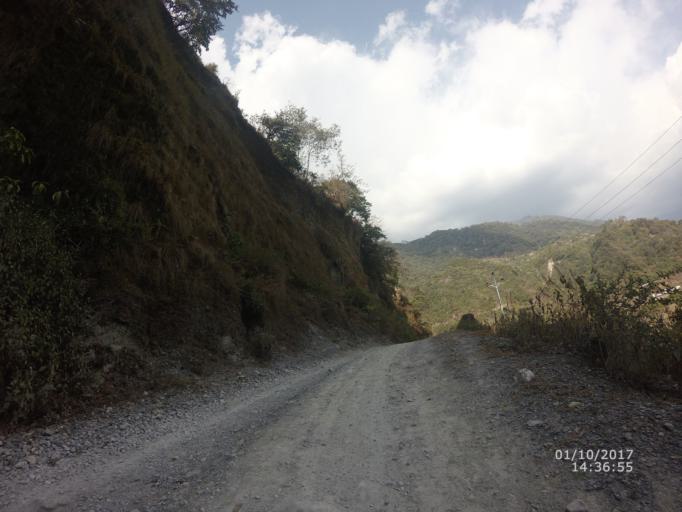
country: NP
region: Western Region
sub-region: Gandaki Zone
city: Pokhara
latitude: 28.3440
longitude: 83.9685
